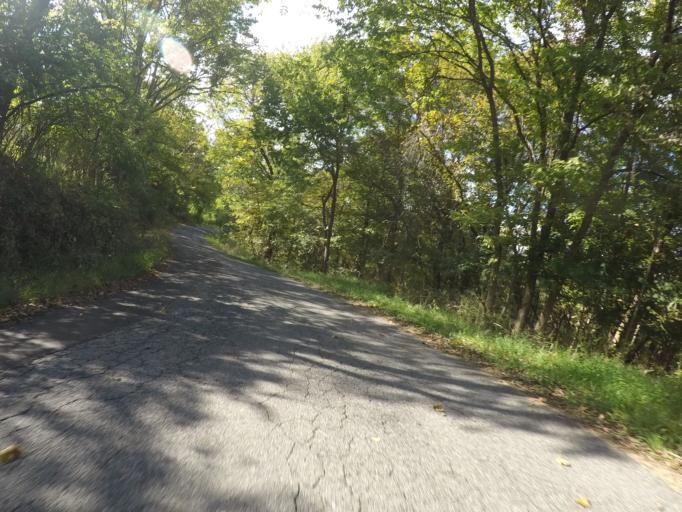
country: US
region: West Virginia
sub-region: Wayne County
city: Lavalette
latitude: 38.3675
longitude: -82.4737
